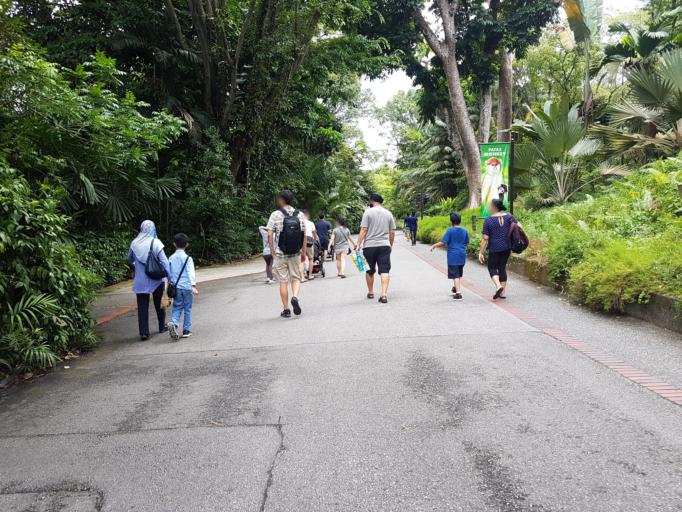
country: MY
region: Johor
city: Johor Bahru
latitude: 1.4048
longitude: 103.7946
